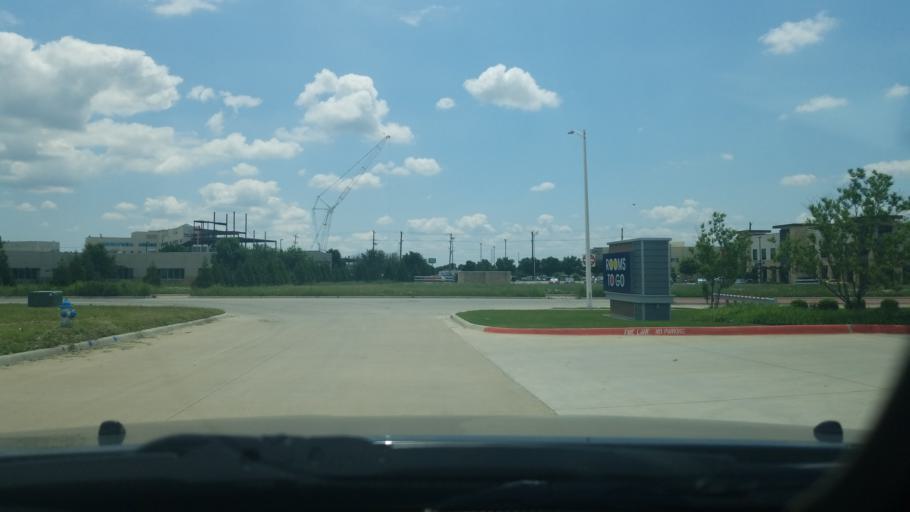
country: US
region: Texas
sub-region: Denton County
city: Denton
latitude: 33.2210
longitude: -97.1691
